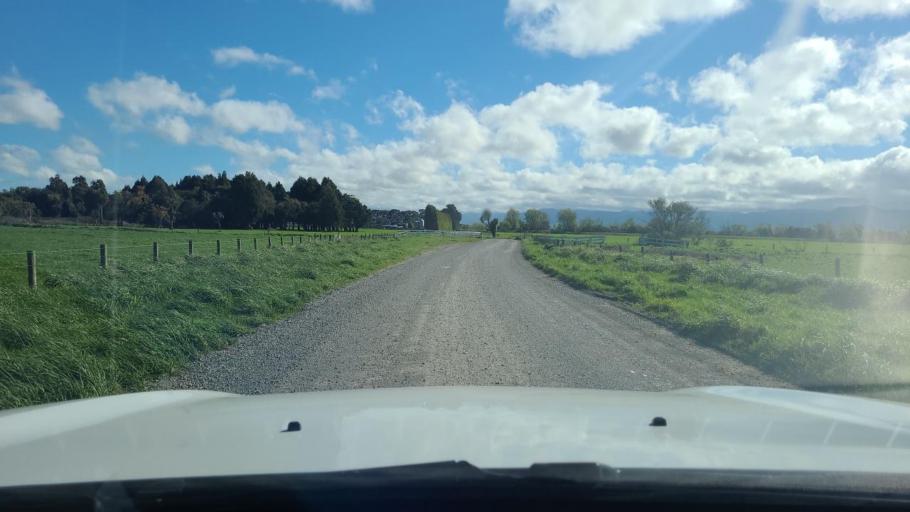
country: NZ
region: Wellington
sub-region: South Wairarapa District
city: Waipawa
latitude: -41.1608
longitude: 175.3628
